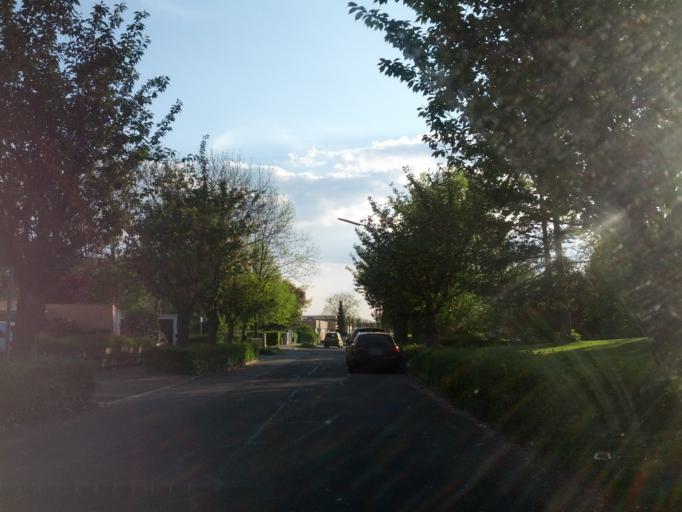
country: DE
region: Baden-Wuerttemberg
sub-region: Freiburg Region
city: Emmendingen
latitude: 48.1073
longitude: 7.8650
